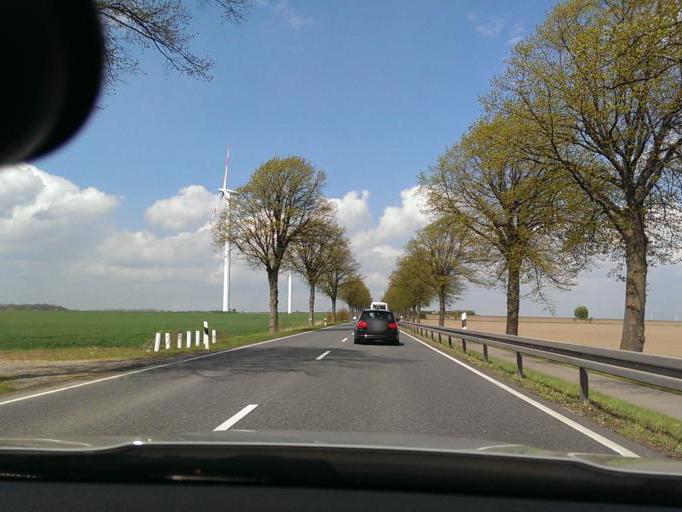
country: DE
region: Lower Saxony
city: Nordstemmen
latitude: 52.1882
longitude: 9.7462
